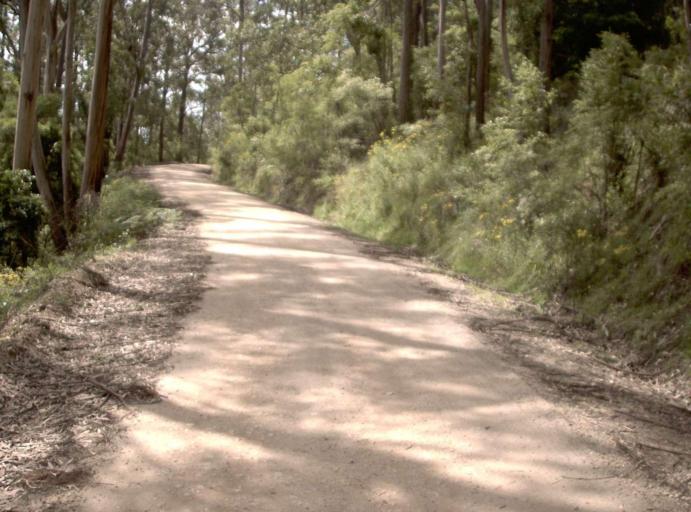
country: AU
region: Victoria
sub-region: East Gippsland
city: Lakes Entrance
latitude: -37.6188
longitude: 148.6996
